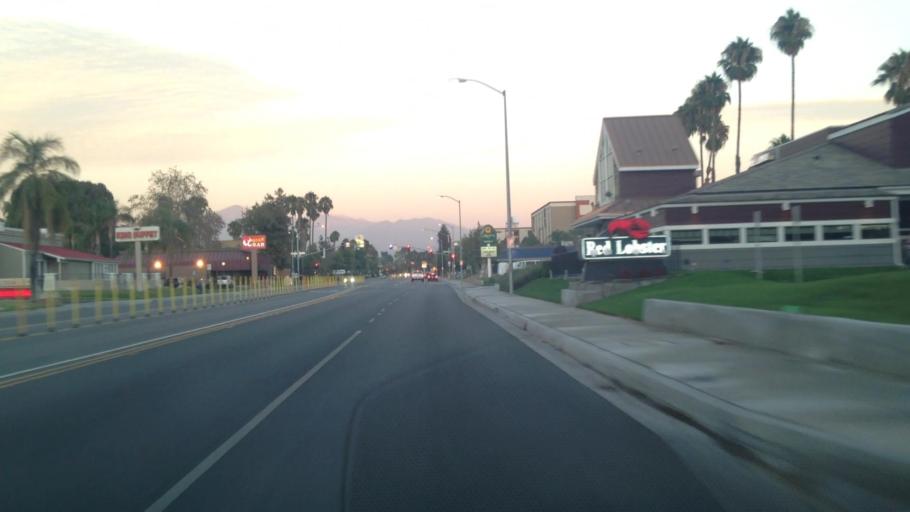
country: US
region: California
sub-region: San Bernardino County
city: Loma Linda
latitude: 34.0657
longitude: -117.2843
